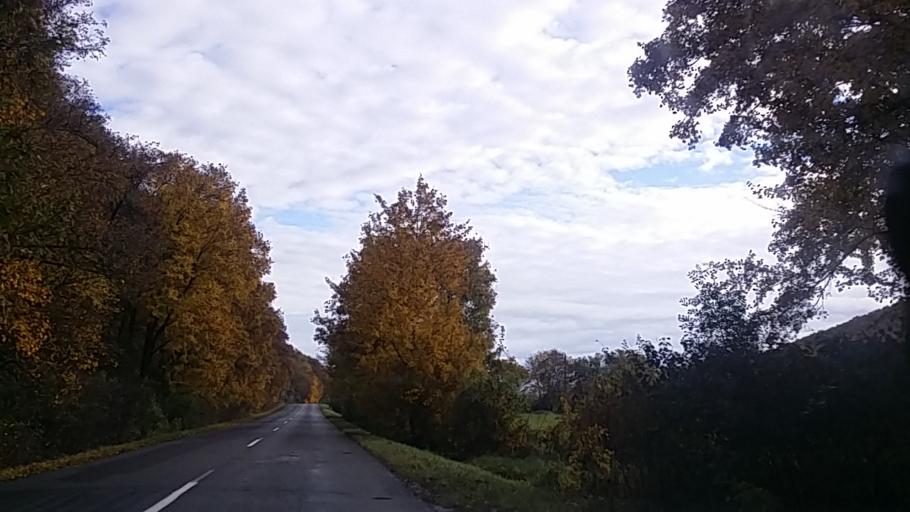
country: HU
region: Heves
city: Szilvasvarad
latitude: 48.1492
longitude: 20.4521
